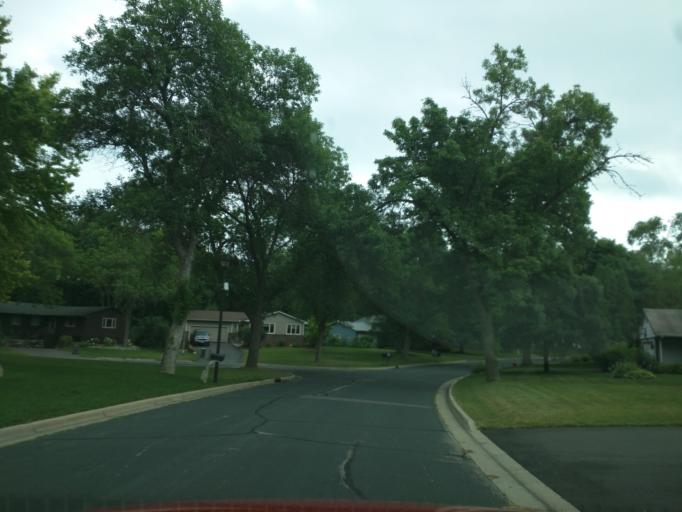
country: US
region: Minnesota
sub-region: Carver County
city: Chanhassen
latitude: 44.8598
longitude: -93.5232
